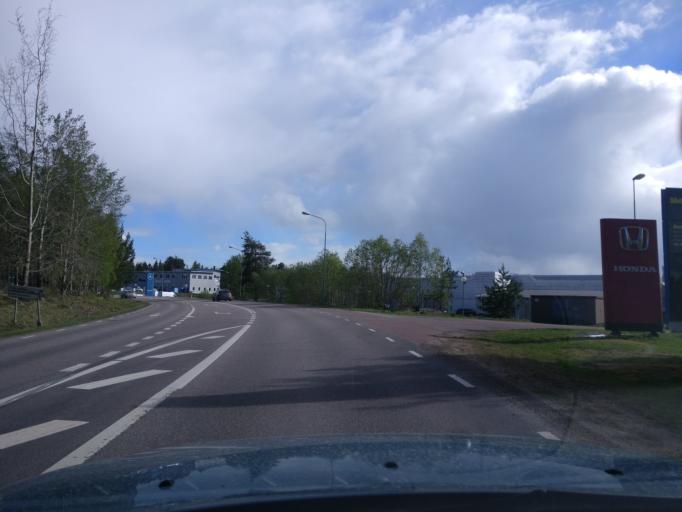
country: SE
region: Vaermland
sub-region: Hammaro Kommun
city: Skoghall
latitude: 59.3812
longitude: 13.4318
